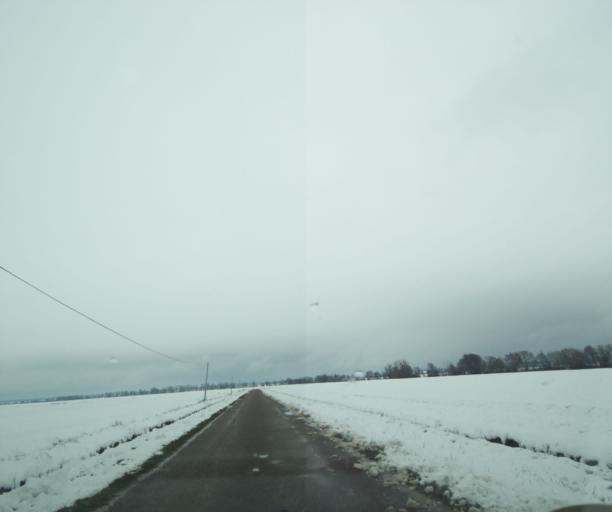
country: FR
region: Champagne-Ardenne
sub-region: Departement de la Haute-Marne
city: Montier-en-Der
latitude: 48.4288
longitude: 4.7890
